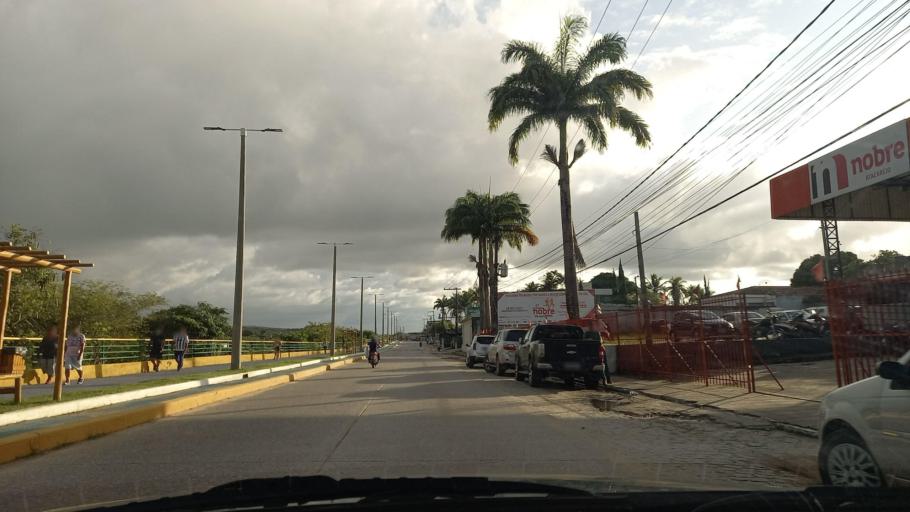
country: BR
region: Pernambuco
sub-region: Palmares
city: Palmares
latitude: -8.6796
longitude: -35.5799
